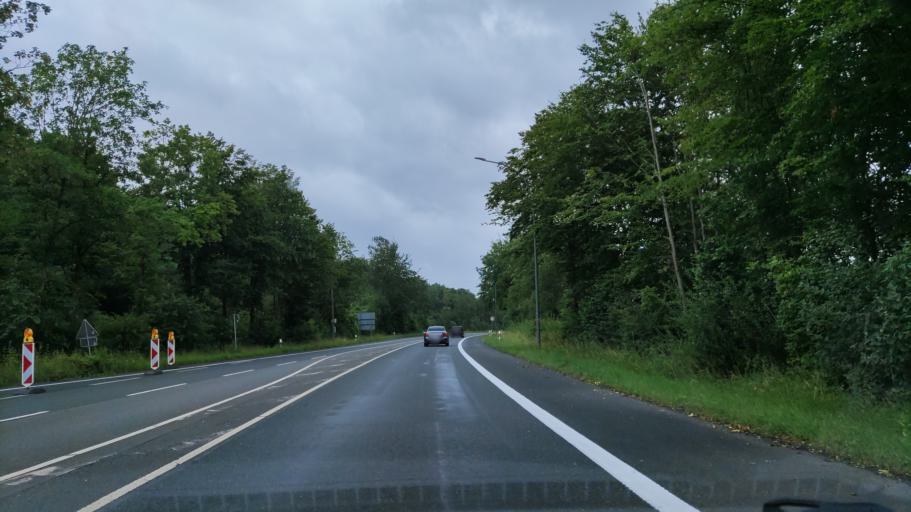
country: DE
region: North Rhine-Westphalia
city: Ahlen
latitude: 51.7405
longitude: 7.8818
